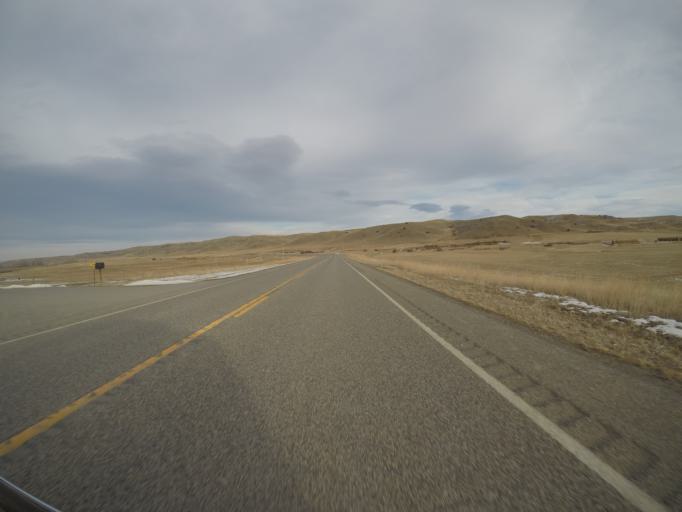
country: US
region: Montana
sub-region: Stillwater County
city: Absarokee
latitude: 45.4417
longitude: -109.4517
